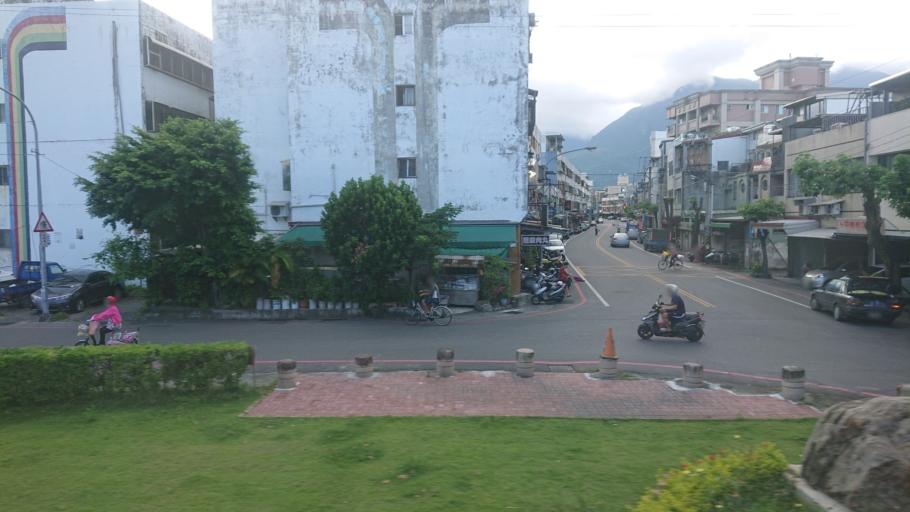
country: TW
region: Taiwan
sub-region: Hualien
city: Hualian
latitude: 23.9869
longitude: 121.5979
